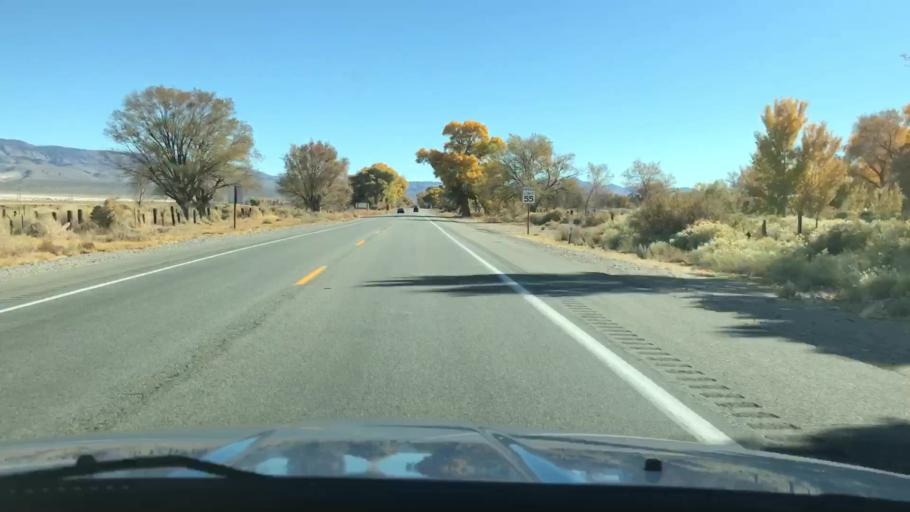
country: US
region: California
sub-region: Inyo County
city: Lone Pine
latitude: 36.2917
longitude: -118.0160
